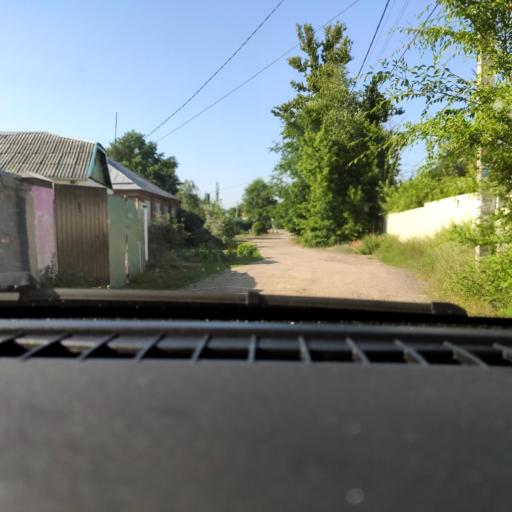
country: RU
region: Voronezj
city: Voronezh
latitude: 51.7309
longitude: 39.2650
